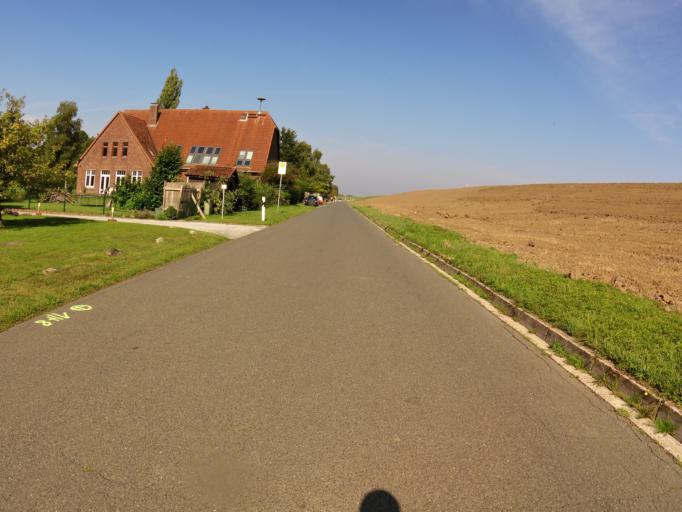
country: DE
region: Lower Saxony
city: Neuenkirchen
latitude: 53.2016
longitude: 8.4953
